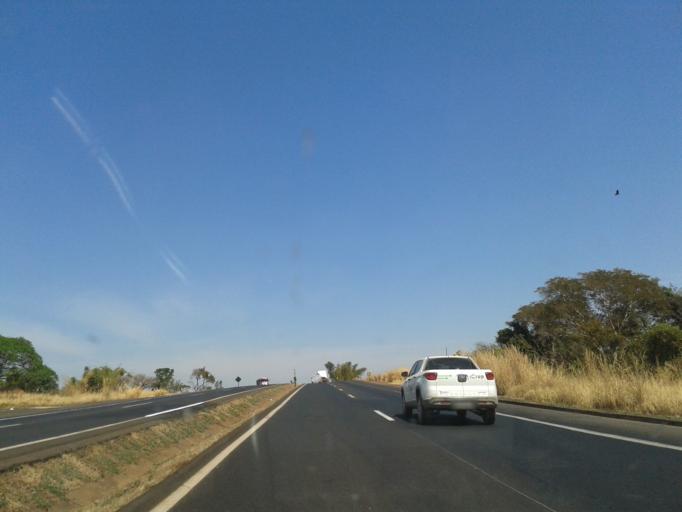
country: BR
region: Minas Gerais
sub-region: Monte Alegre De Minas
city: Monte Alegre de Minas
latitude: -18.8398
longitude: -49.0926
